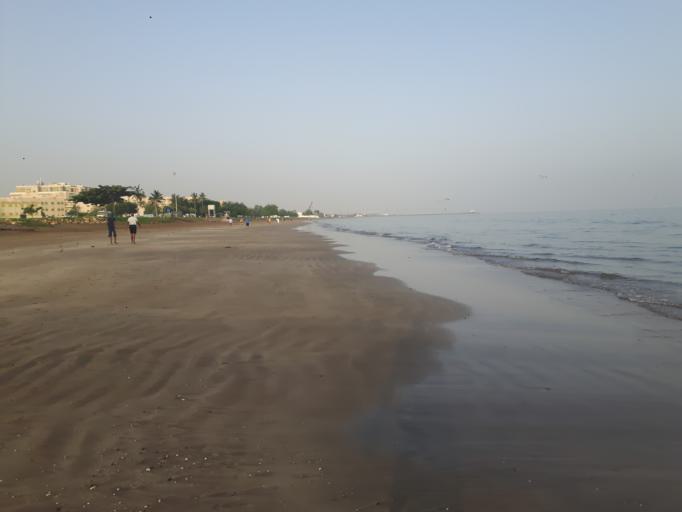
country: OM
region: Muhafazat Masqat
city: Bawshar
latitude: 23.6116
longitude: 58.4482
